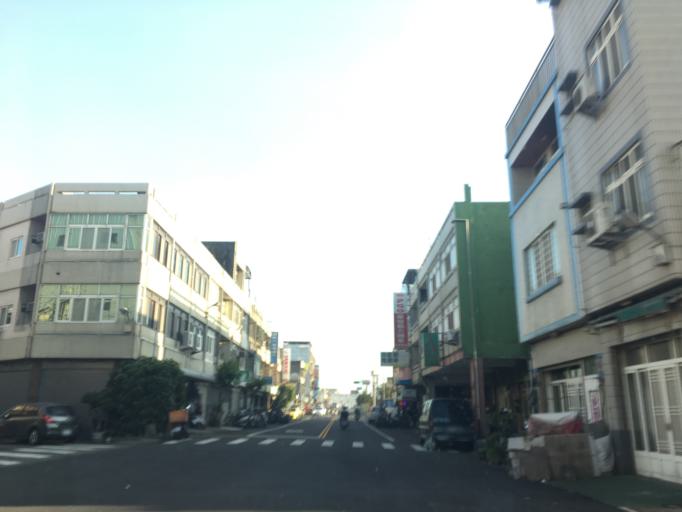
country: TW
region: Taiwan
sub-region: Changhua
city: Chang-hua
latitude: 24.0483
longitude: 120.4370
